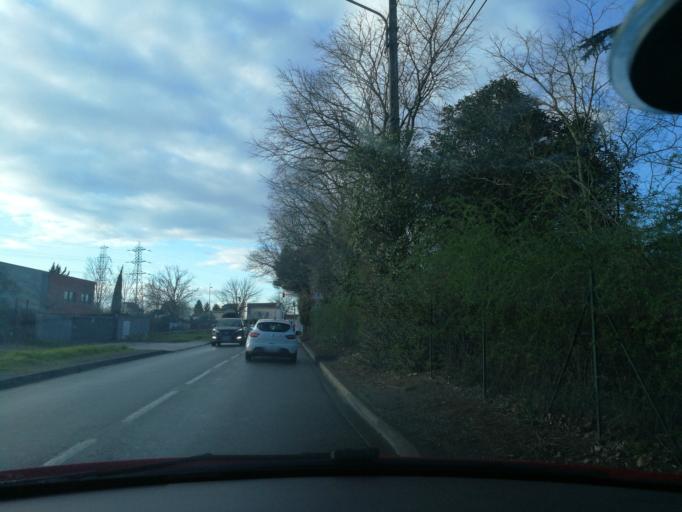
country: FR
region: Midi-Pyrenees
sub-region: Departement de la Haute-Garonne
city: Blagnac
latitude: 43.6419
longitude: 1.4167
